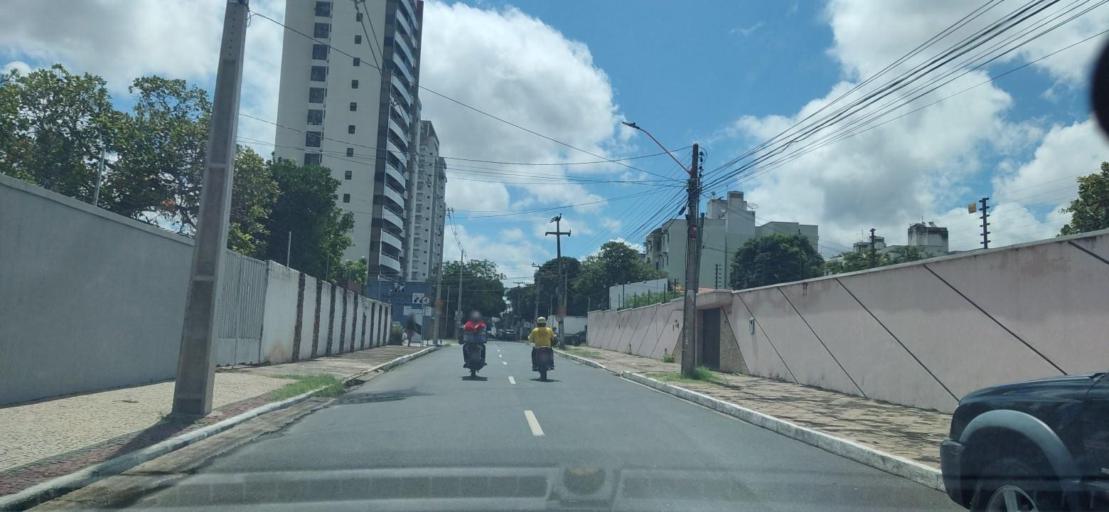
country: BR
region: Piaui
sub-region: Teresina
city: Teresina
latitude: -5.0649
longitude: -42.7833
